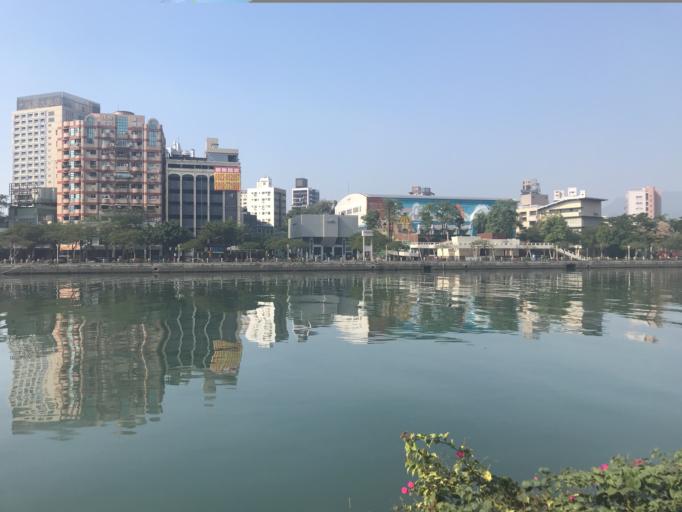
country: TW
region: Kaohsiung
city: Kaohsiung
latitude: 22.6223
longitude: 120.2906
